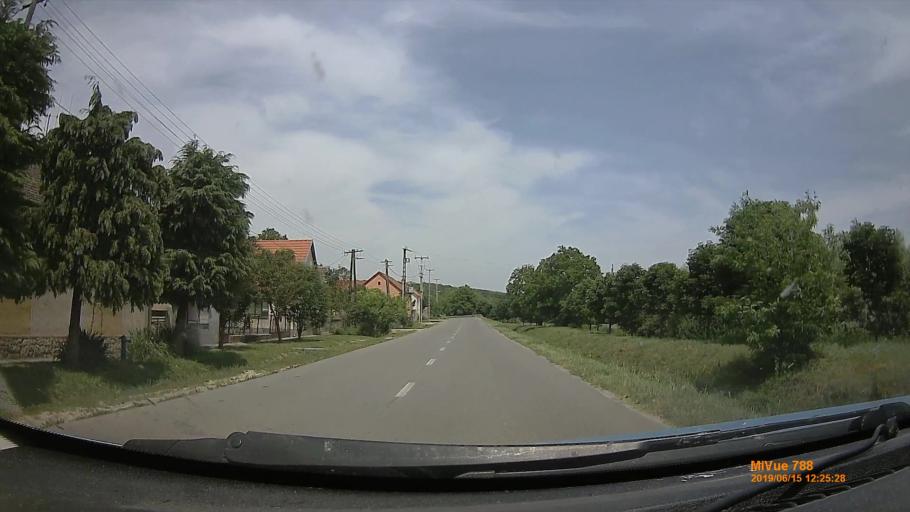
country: HU
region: Baranya
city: Buekkoesd
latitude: 46.1150
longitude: 17.9959
